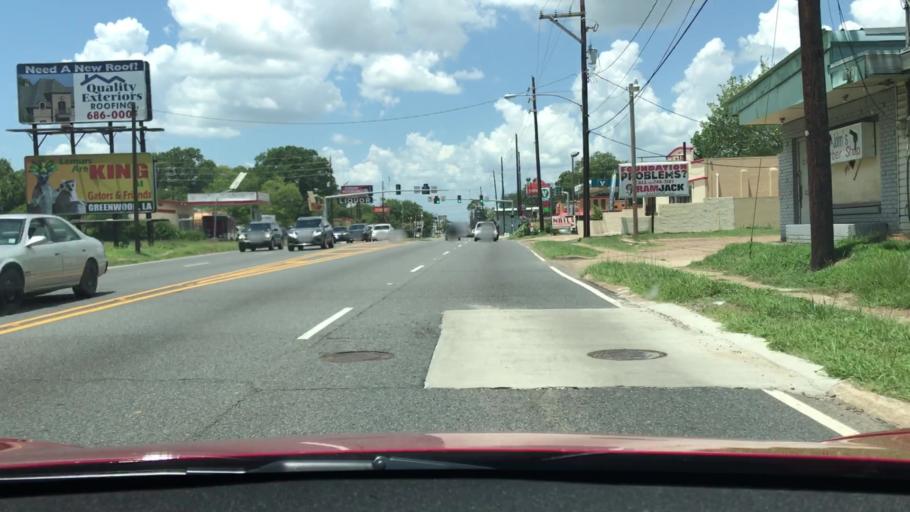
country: US
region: Louisiana
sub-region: Bossier Parish
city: Bossier City
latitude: 32.4421
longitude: -93.7447
